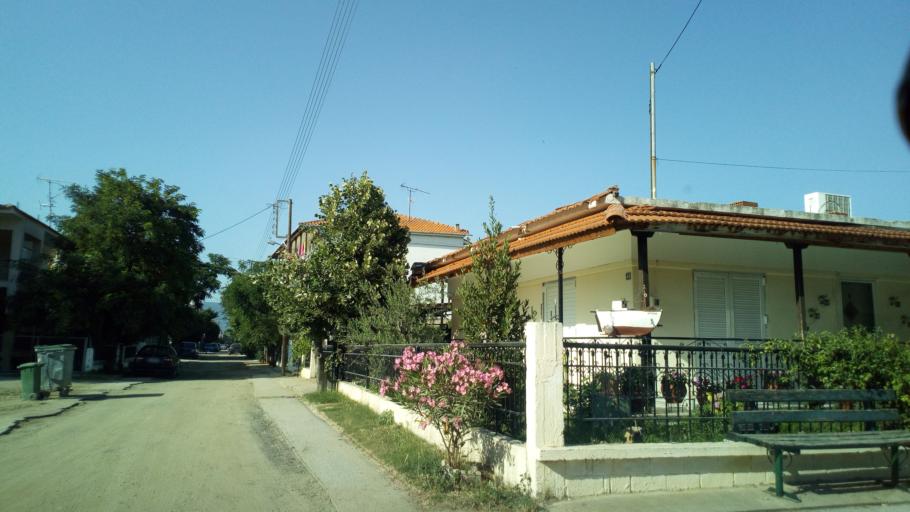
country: GR
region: Central Macedonia
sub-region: Nomos Thessalonikis
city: Nea Vrasna
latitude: 40.7066
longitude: 23.7004
